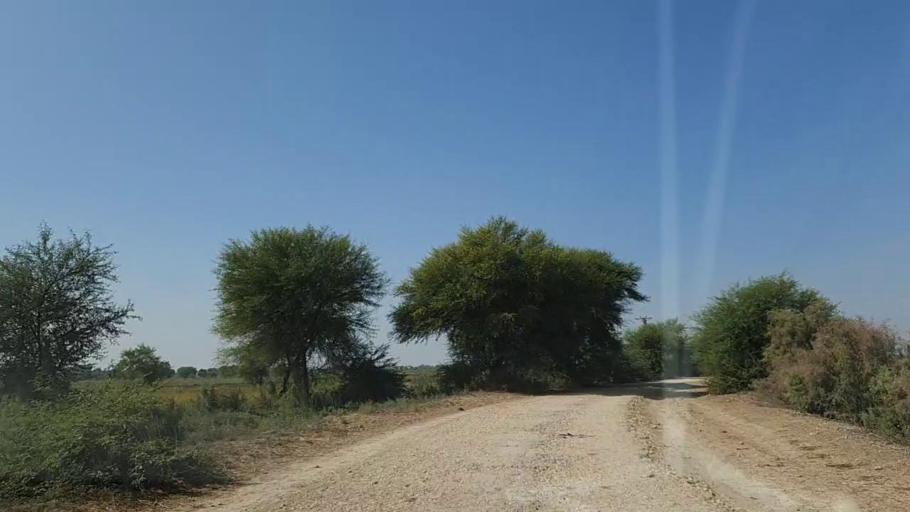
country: PK
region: Sindh
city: Chuhar Jamali
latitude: 24.4197
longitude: 68.0152
